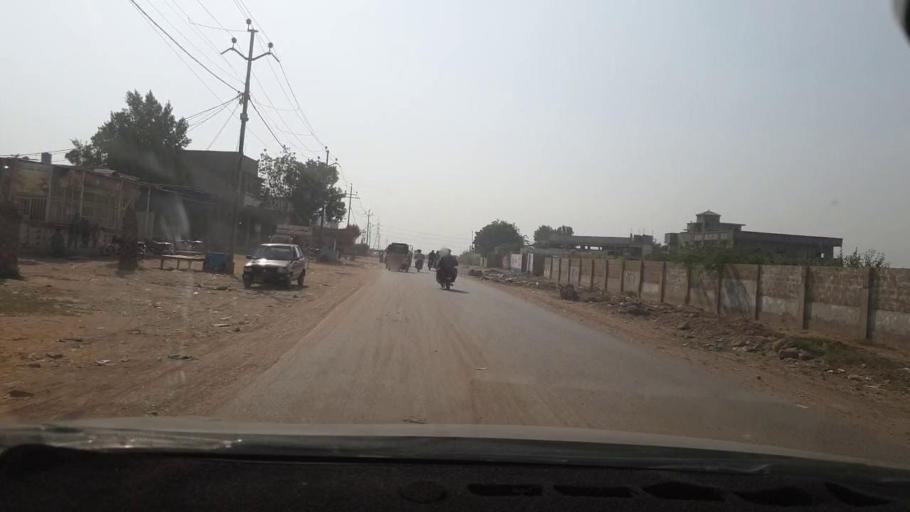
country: PK
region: Sindh
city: Malir Cantonment
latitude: 25.0033
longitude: 67.1515
